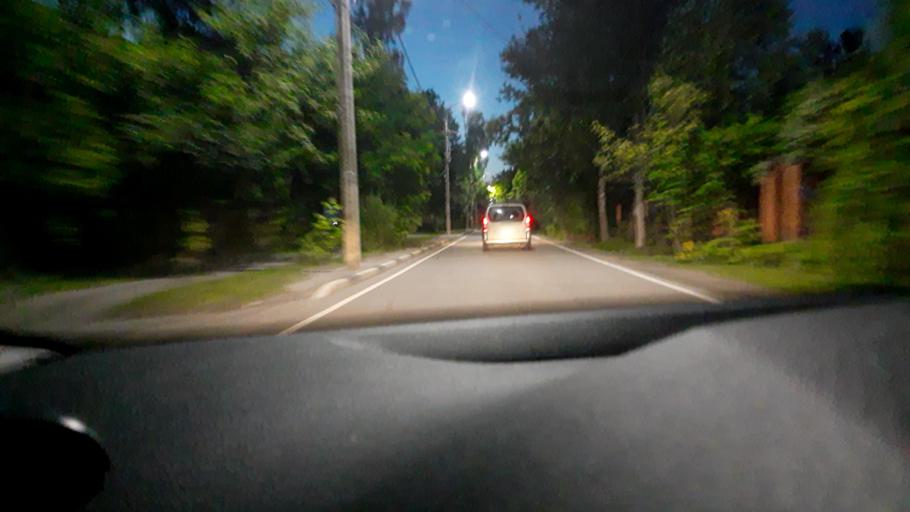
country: RU
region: Moskovskaya
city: Opalikha
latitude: 55.8270
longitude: 37.2474
